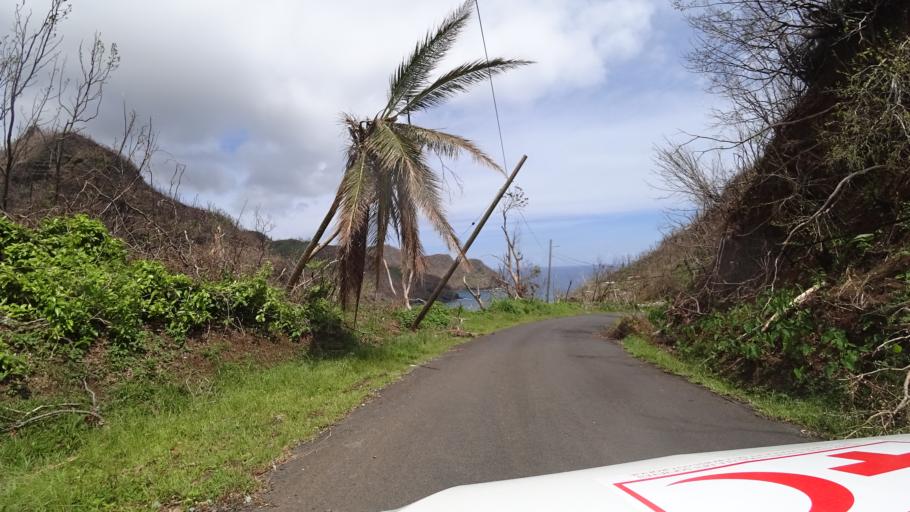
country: DM
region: Saint David
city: Rosalie
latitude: 15.3993
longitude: -61.2577
